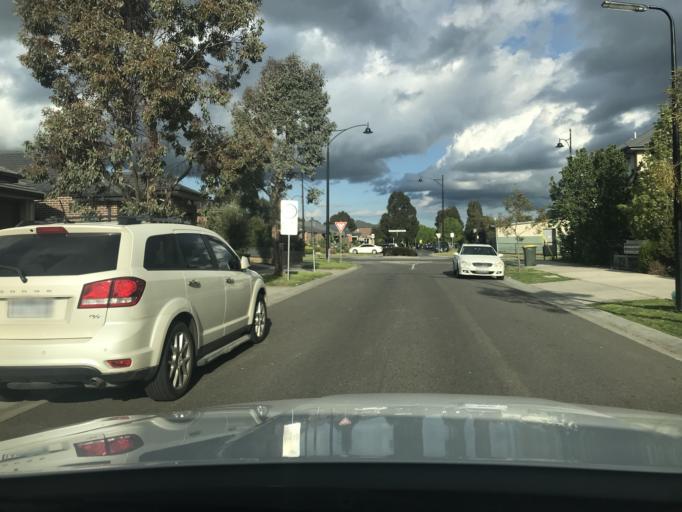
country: AU
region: Victoria
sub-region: Hume
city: Roxburgh Park
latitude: -37.5811
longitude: 144.9040
